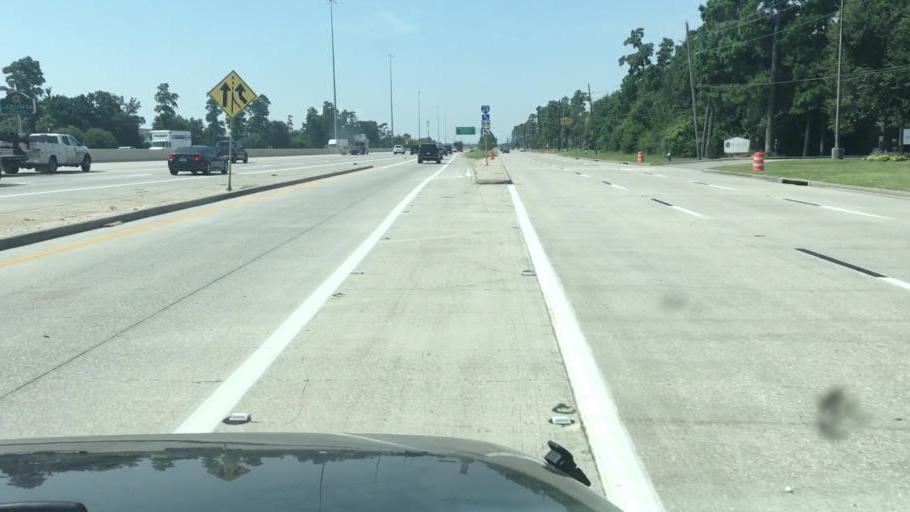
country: US
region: Texas
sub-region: Harris County
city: Humble
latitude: 30.0492
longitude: -95.2562
